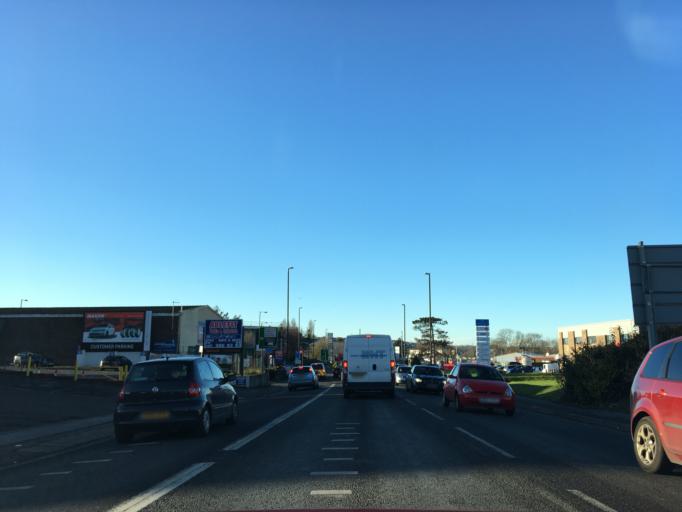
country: GB
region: England
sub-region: Bath and North East Somerset
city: Whitchurch
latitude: 51.4298
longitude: -2.5408
